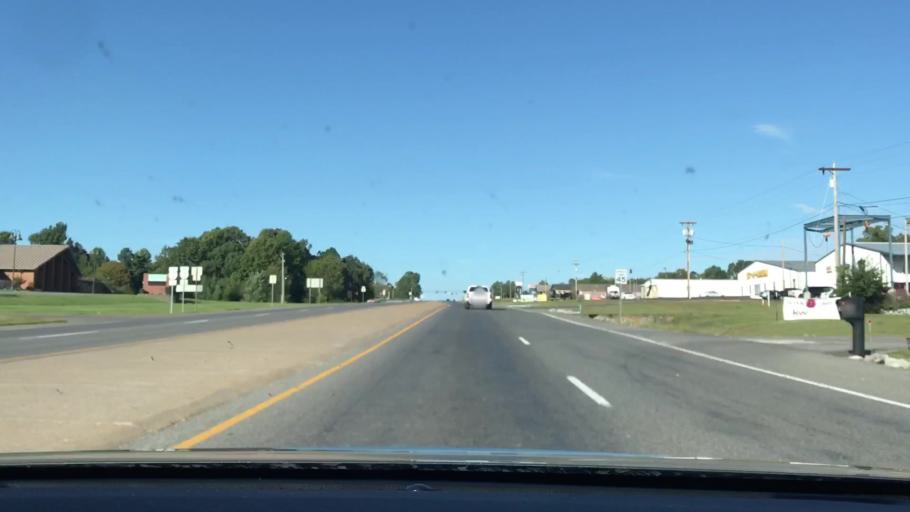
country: US
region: Kentucky
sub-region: Marshall County
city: Calvert City
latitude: 37.0040
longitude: -88.3485
